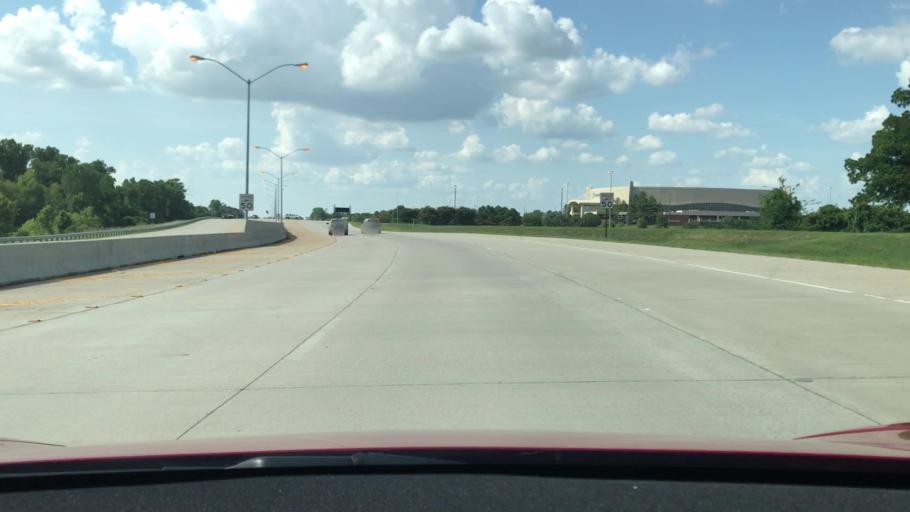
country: US
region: Louisiana
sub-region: Bossier Parish
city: Bossier City
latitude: 32.4596
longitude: -93.6753
